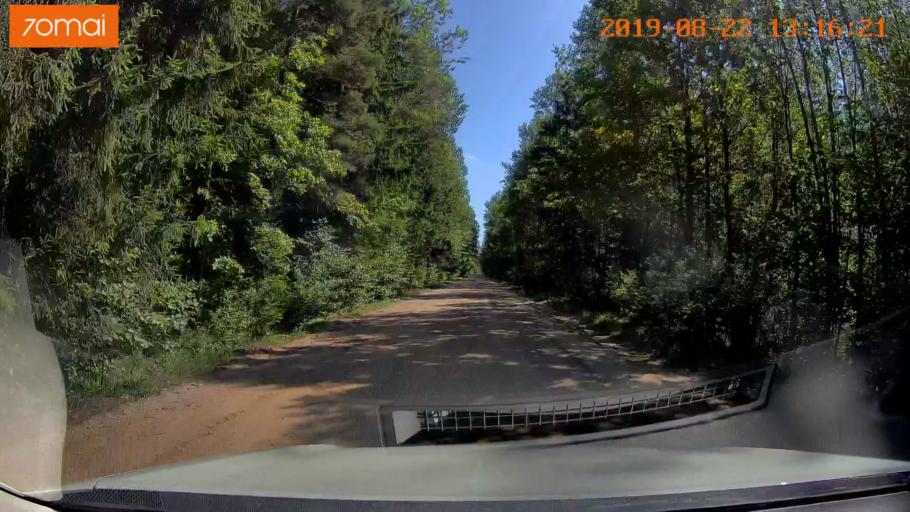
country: BY
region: Minsk
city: Prawdzinski
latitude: 53.2563
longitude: 27.9101
